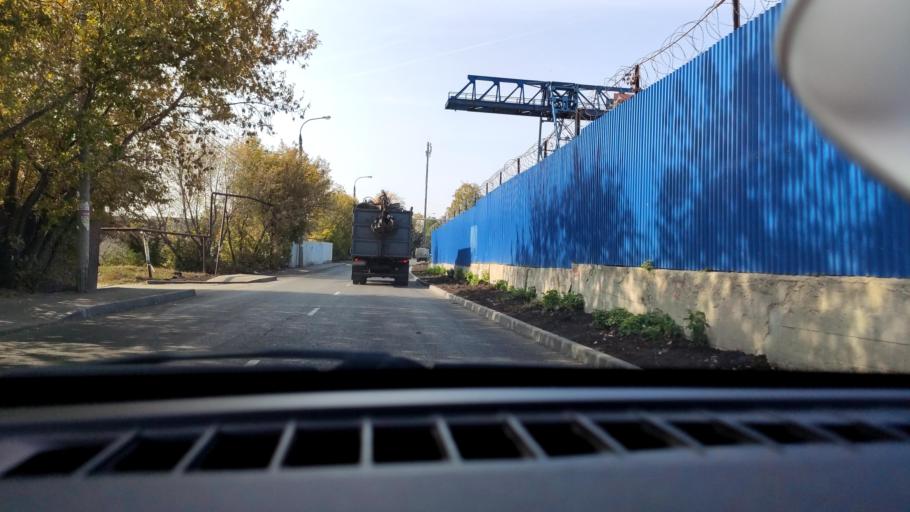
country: RU
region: Samara
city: Samara
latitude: 53.1798
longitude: 50.1389
